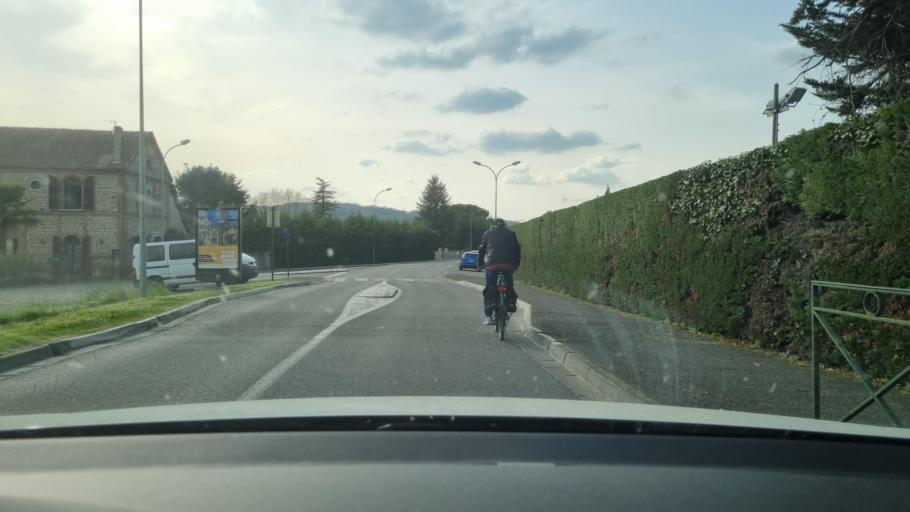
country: FR
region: Midi-Pyrenees
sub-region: Departement des Hautes-Pyrenees
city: Vic-en-Bigorre
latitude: 43.3850
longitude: 0.0487
